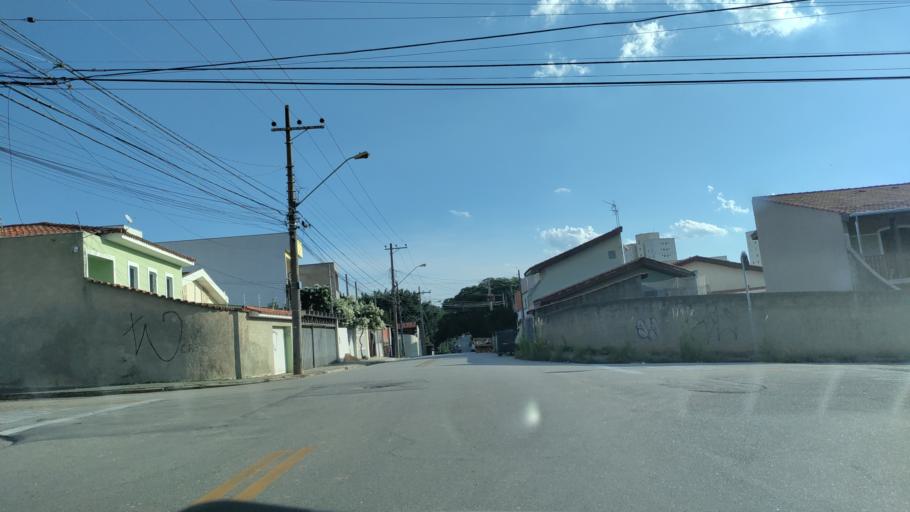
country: BR
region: Sao Paulo
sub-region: Sorocaba
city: Sorocaba
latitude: -23.4768
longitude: -47.4511
